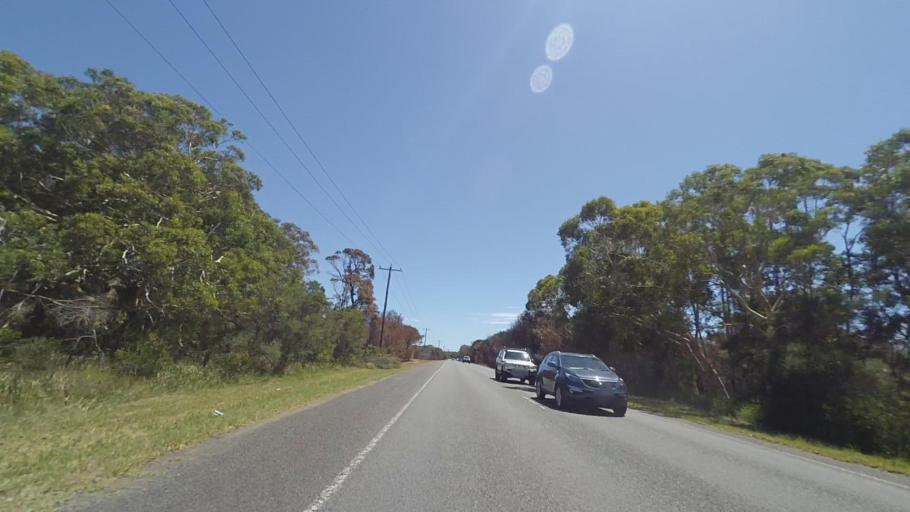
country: AU
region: New South Wales
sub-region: Port Stephens Shire
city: Medowie
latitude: -32.7886
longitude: 151.8552
